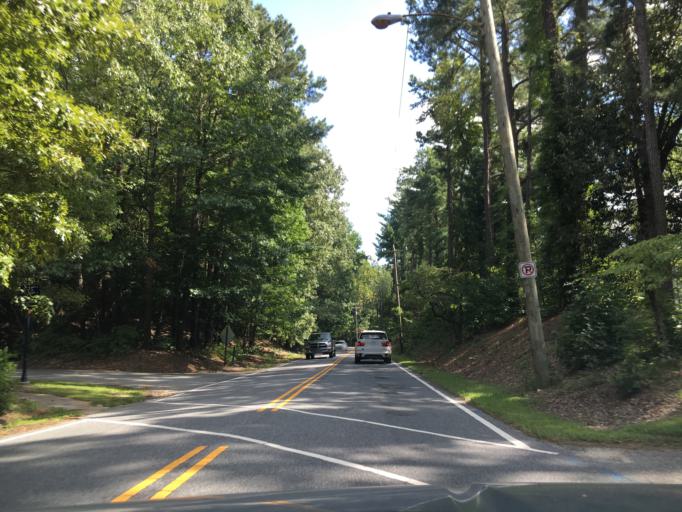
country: US
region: Virginia
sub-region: Henrico County
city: Tuckahoe
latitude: 37.5811
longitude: -77.5353
